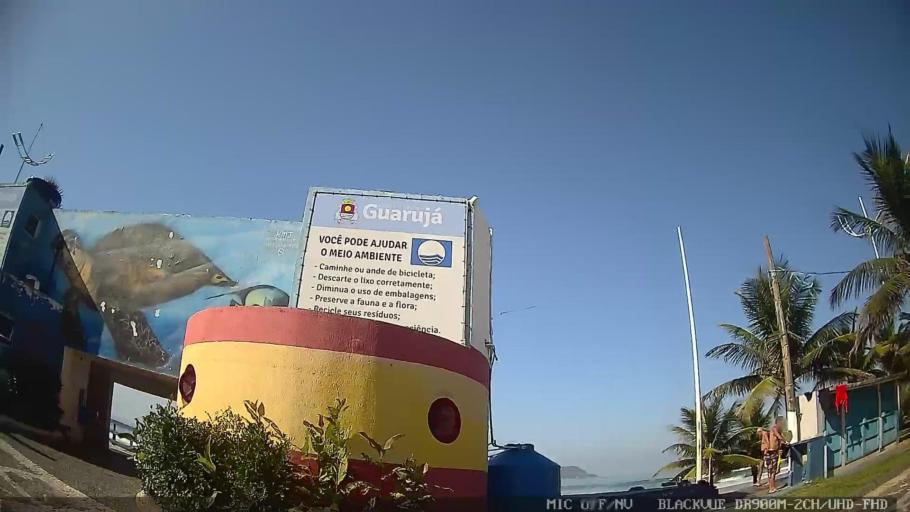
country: BR
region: Sao Paulo
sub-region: Guaruja
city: Guaruja
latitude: -24.0142
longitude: -46.2736
